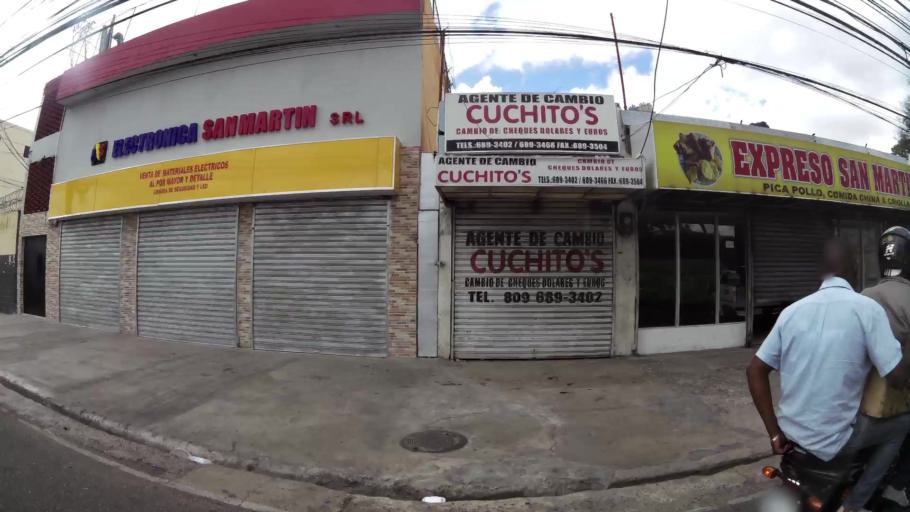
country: DO
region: Nacional
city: San Carlos
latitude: 18.4799
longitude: -69.9016
